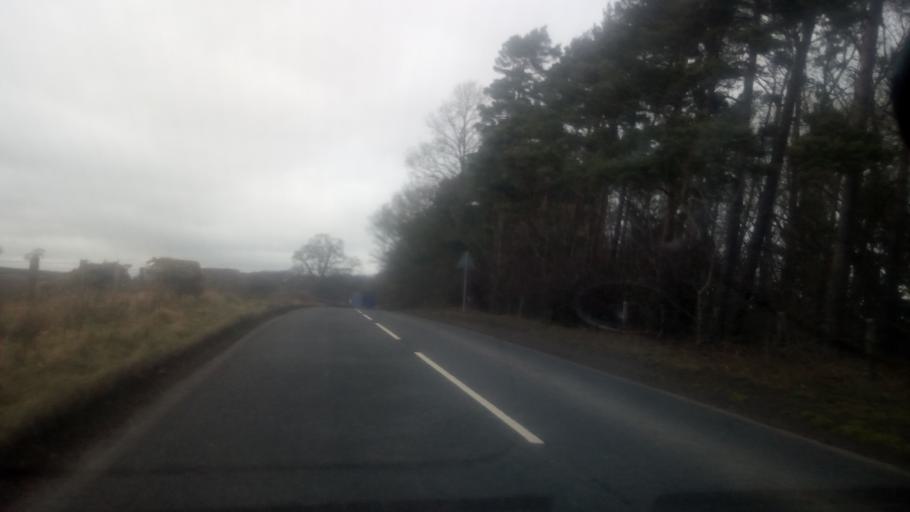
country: GB
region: Scotland
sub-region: The Scottish Borders
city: Kelso
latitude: 55.5911
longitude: -2.4732
